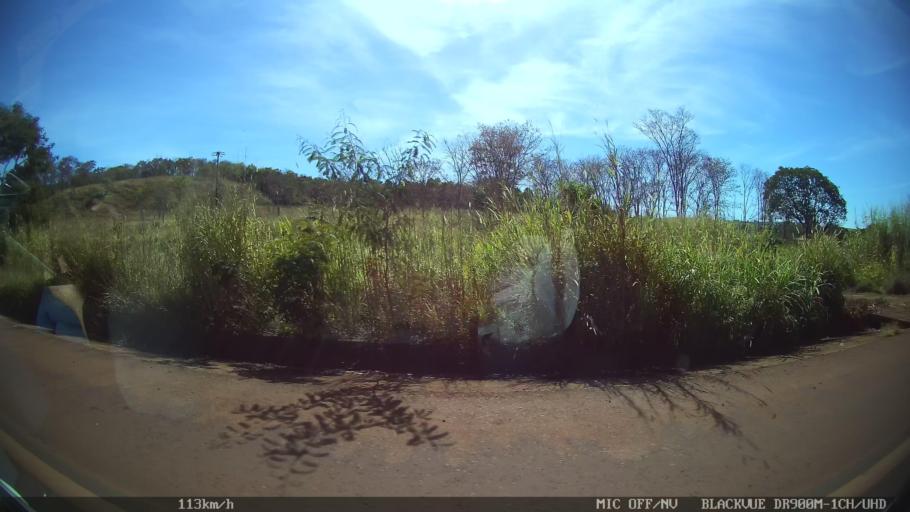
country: BR
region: Sao Paulo
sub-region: Sao Joaquim Da Barra
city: Sao Joaquim da Barra
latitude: -20.5528
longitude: -47.6632
